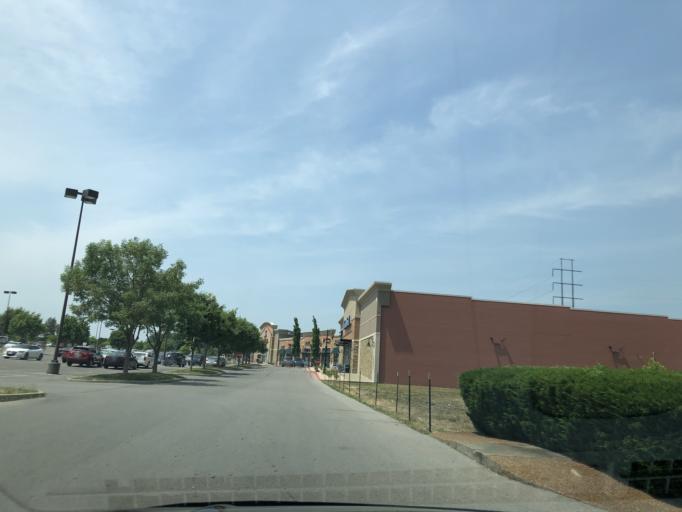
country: US
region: Tennessee
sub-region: Rutherford County
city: La Vergne
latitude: 36.0512
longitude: -86.6137
